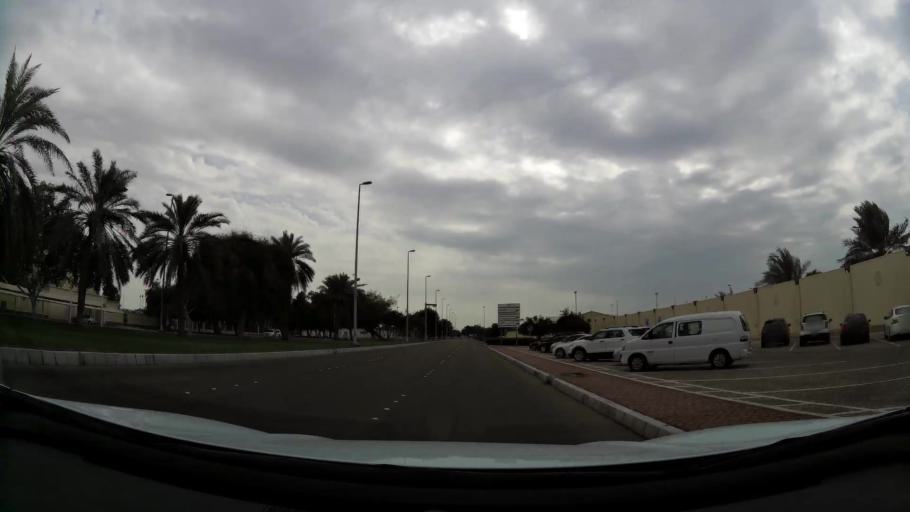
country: AE
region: Abu Dhabi
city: Abu Dhabi
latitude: 24.4344
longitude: 54.4209
